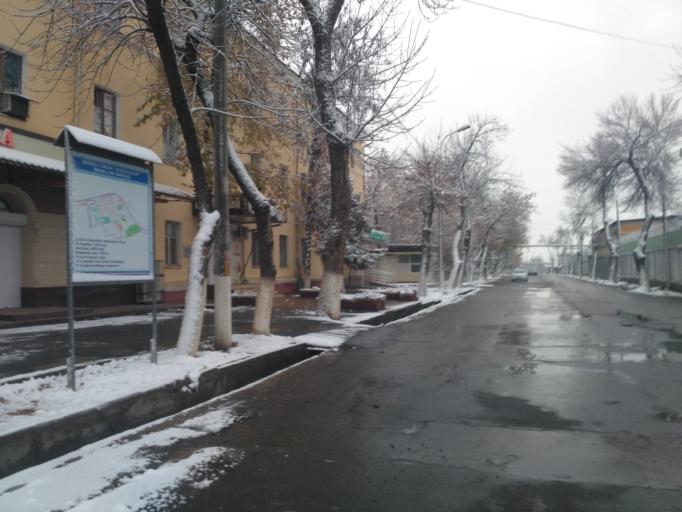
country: UZ
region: Toshkent Shahri
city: Tashkent
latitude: 41.2697
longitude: 69.2766
